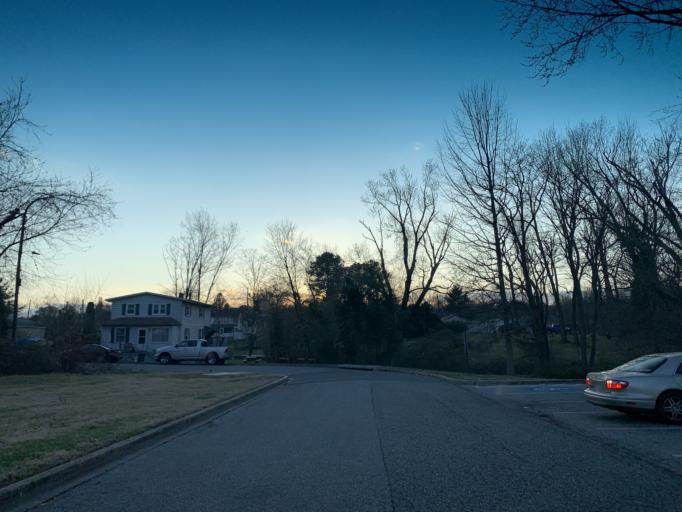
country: US
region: Maryland
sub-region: Harford County
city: Havre de Grace
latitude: 39.5560
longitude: -76.0950
